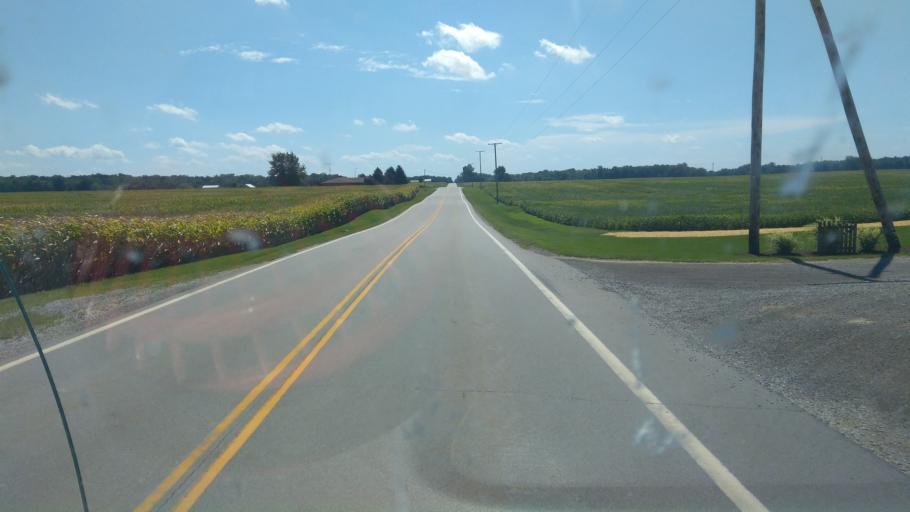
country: US
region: Ohio
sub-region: Wyandot County
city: Upper Sandusky
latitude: 40.7936
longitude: -83.1308
